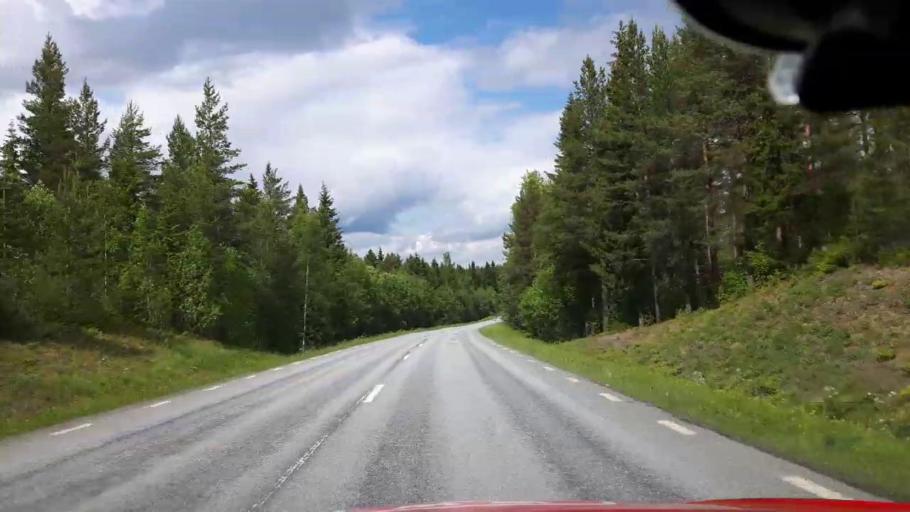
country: SE
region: Jaemtland
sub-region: Krokoms Kommun
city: Krokom
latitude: 63.3711
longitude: 14.3875
